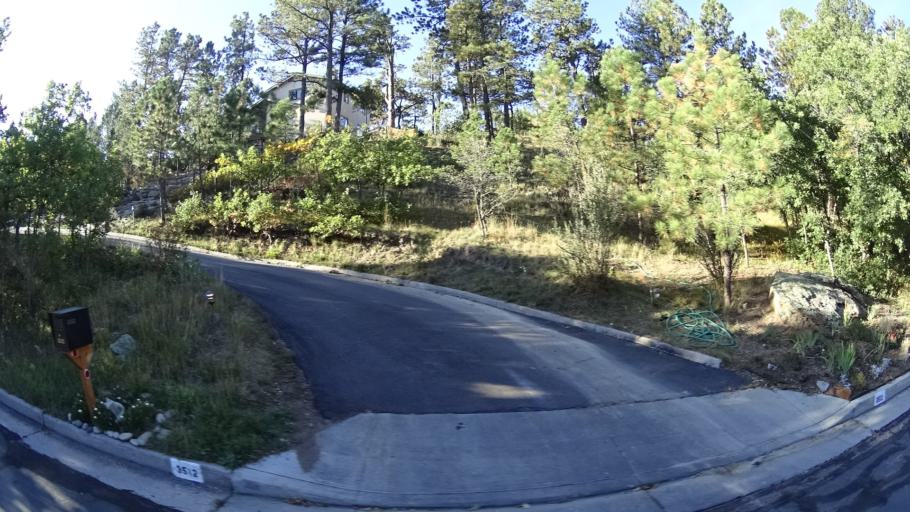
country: US
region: Colorado
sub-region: El Paso County
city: Cimarron Hills
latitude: 38.8825
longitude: -104.7673
